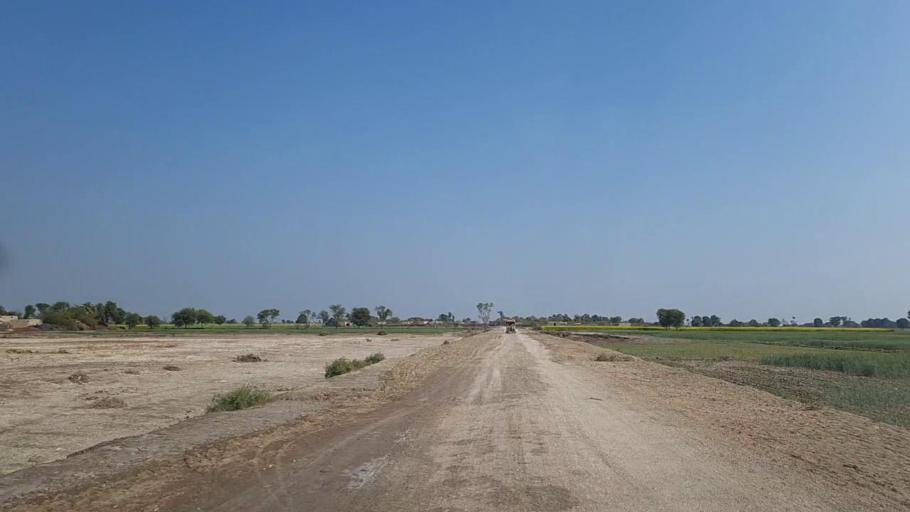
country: PK
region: Sindh
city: Jam Sahib
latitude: 26.2551
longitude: 68.5723
